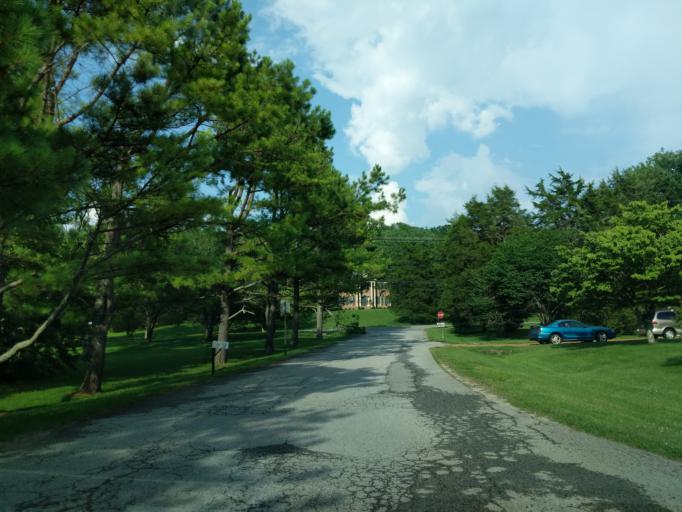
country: US
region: Tennessee
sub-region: Davidson County
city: Belle Meade
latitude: 36.0362
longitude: -86.9527
